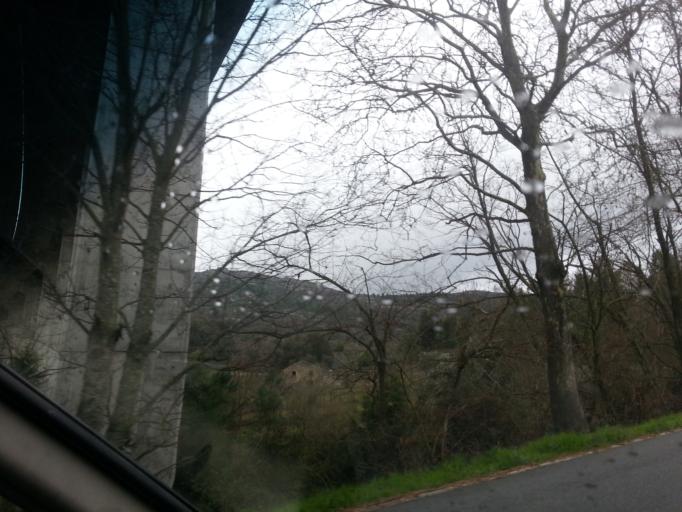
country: PT
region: Guarda
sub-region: Fornos de Algodres
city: Fornos de Algodres
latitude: 40.6244
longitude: -7.5881
